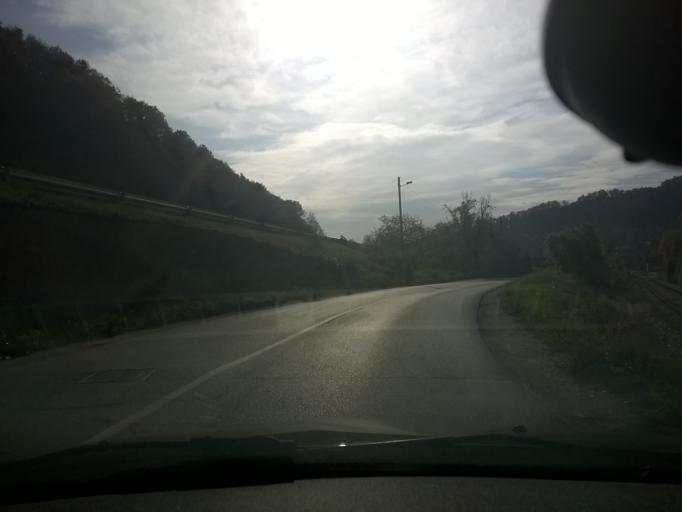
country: HR
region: Krapinsko-Zagorska
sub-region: Grad Krapina
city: Krapina
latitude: 46.1734
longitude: 15.8643
